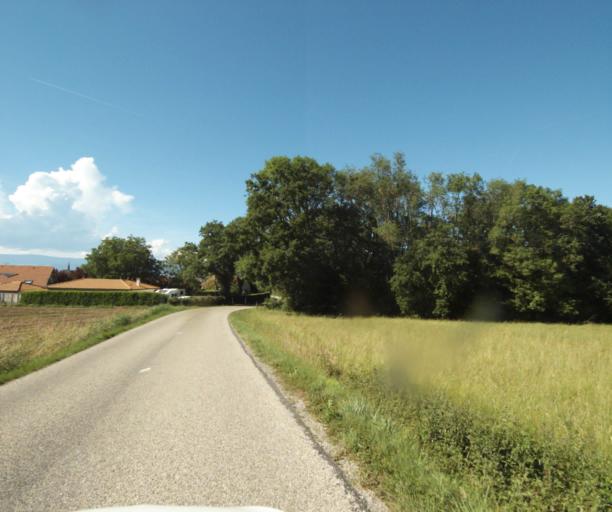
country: FR
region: Rhone-Alpes
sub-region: Departement de la Haute-Savoie
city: Sciez
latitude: 46.3234
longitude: 6.3814
